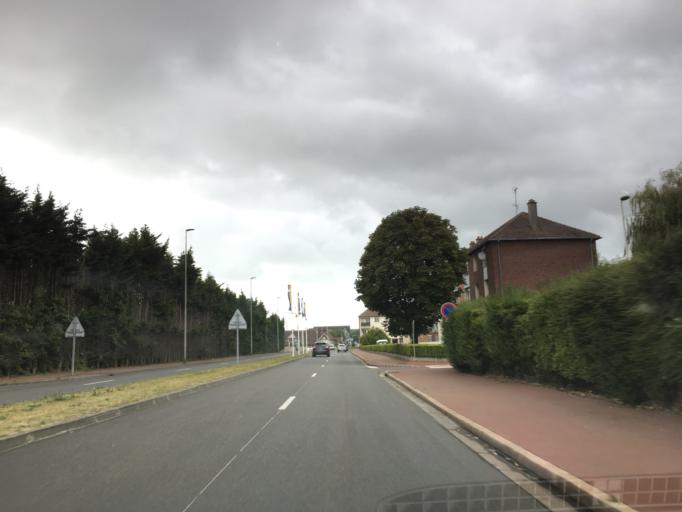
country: FR
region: Lower Normandy
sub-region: Departement du Calvados
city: Trouville-sur-Mer
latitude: 49.3566
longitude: 0.0876
